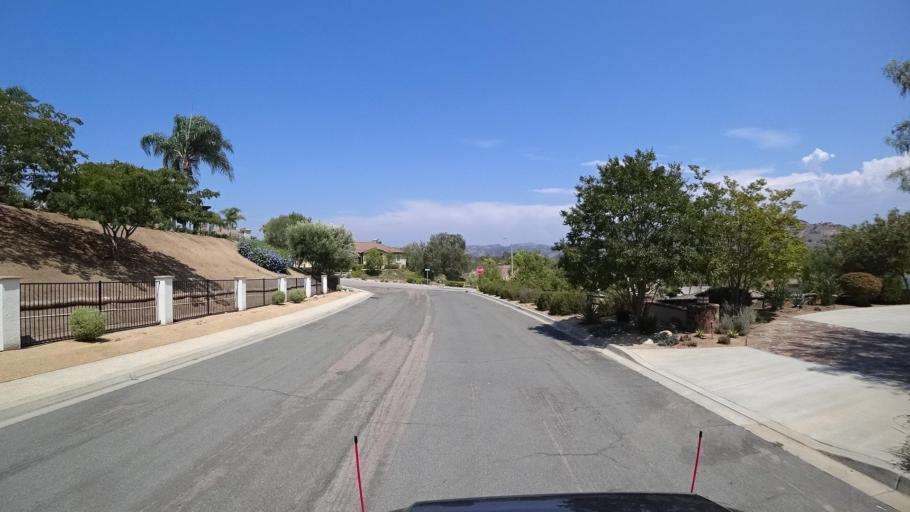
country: US
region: California
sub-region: San Diego County
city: Bonsall
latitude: 33.3153
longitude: -117.2013
